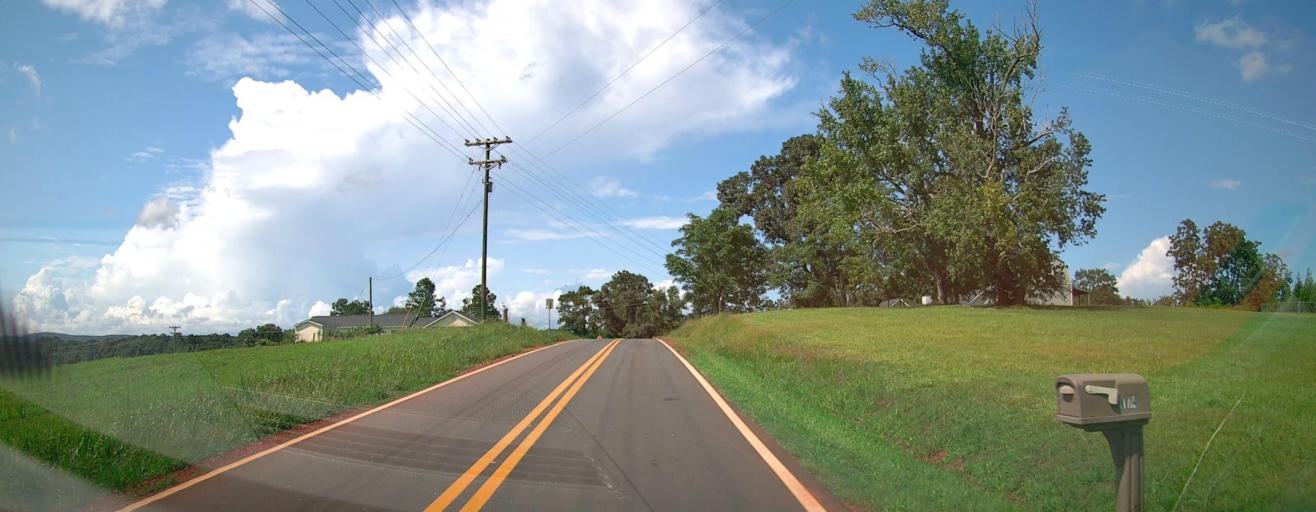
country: US
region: Georgia
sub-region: Upson County
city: Hannahs Mill
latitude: 32.9490
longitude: -84.2902
